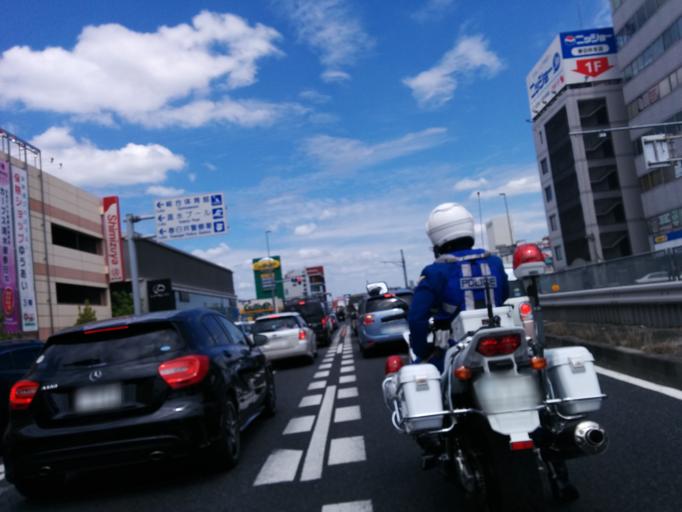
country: JP
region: Aichi
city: Kasugai
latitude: 35.2490
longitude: 136.9718
